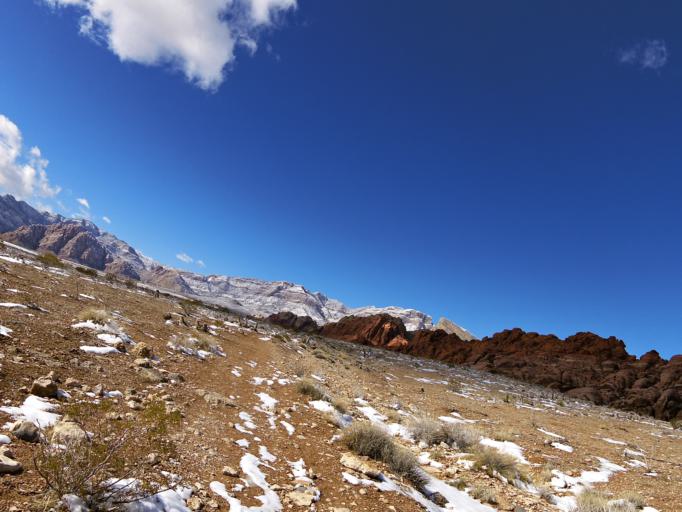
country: US
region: Nevada
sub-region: Clark County
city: Summerlin South
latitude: 36.1423
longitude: -115.4270
